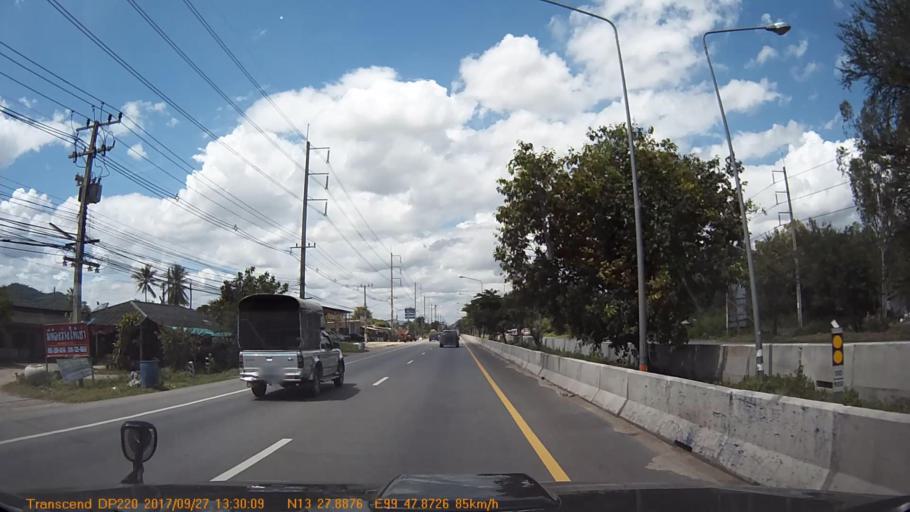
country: TH
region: Ratchaburi
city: Ratchaburi
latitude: 13.4649
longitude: 99.7979
